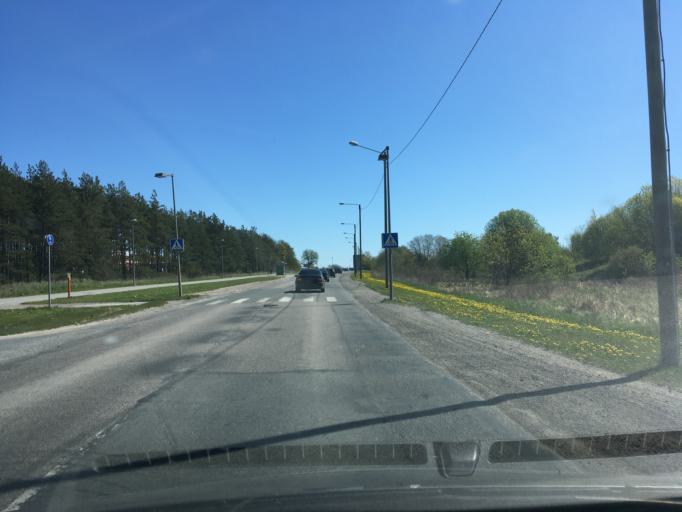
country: EE
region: Harju
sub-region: Joelaehtme vald
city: Loo
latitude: 59.4608
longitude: 24.9236
